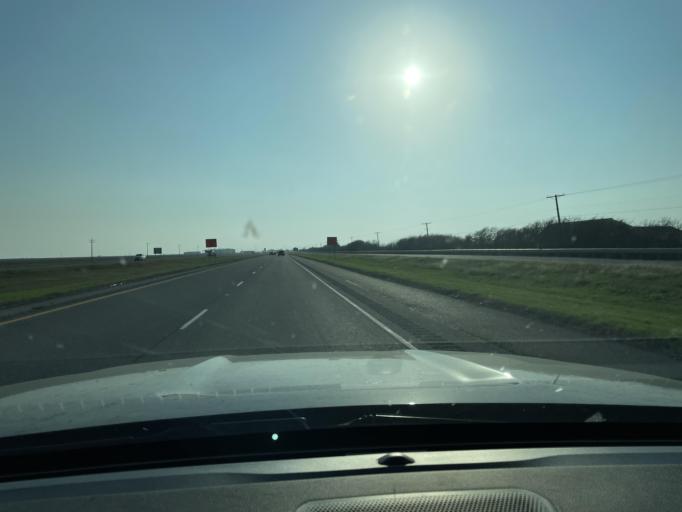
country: US
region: Texas
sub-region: Nueces County
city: Robstown
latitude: 27.7531
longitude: -97.6894
